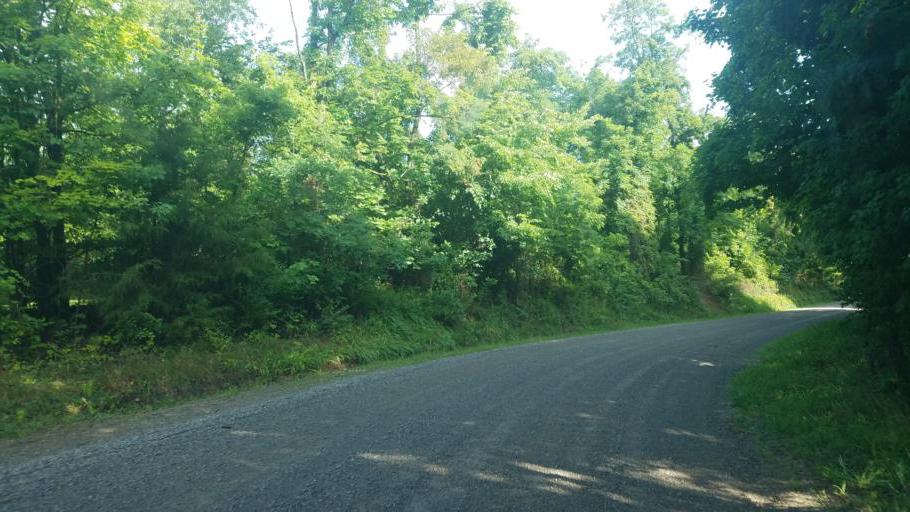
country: US
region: Ohio
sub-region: Gallia County
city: Gallipolis
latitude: 38.7458
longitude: -82.3507
